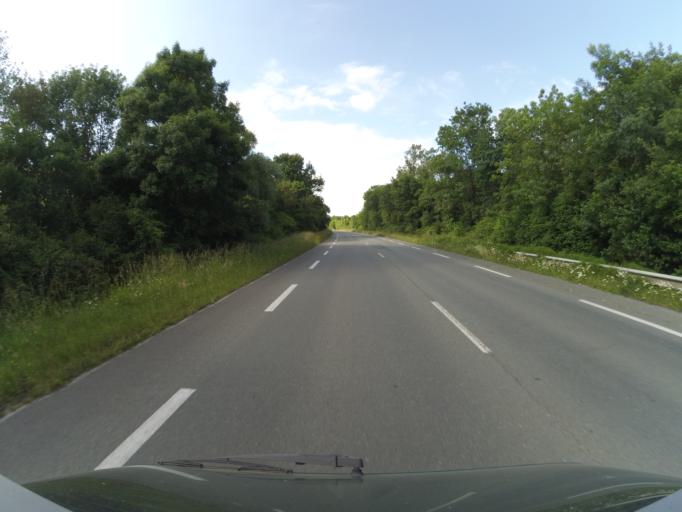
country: FR
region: Poitou-Charentes
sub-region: Departement de la Charente-Maritime
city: Saint-Agnant
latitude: 45.8155
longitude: -0.9310
